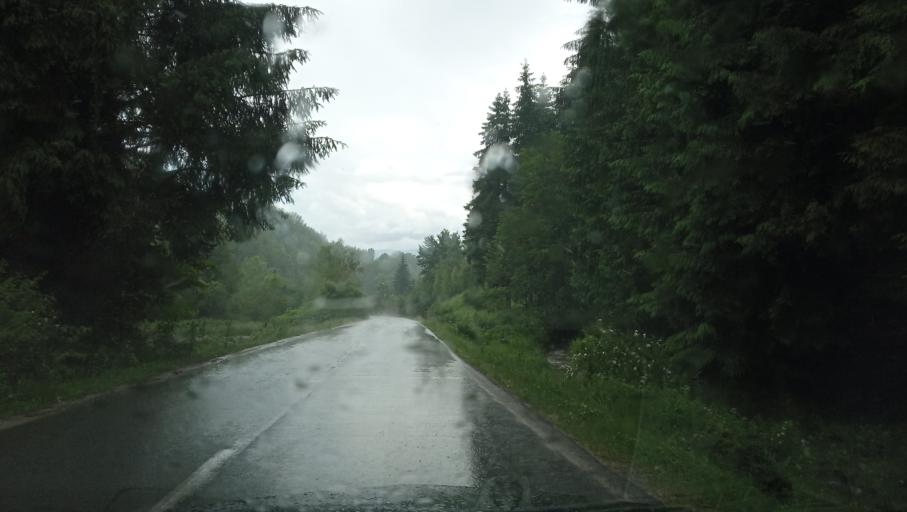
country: RO
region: Hunedoara
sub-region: Oras Petrila
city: Petrila
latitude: 45.3964
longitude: 23.4205
